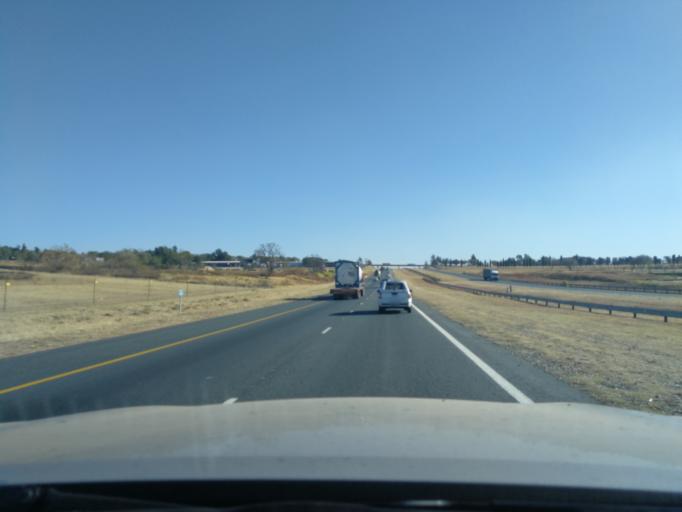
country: ZA
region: Gauteng
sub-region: West Rand District Municipality
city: Muldersdriseloop
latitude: -26.0095
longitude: 27.8885
